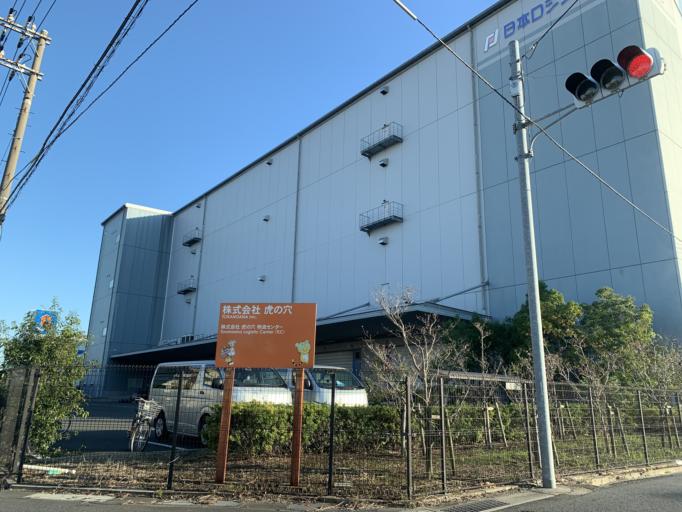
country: JP
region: Tokyo
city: Urayasu
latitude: 35.7080
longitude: 139.9293
